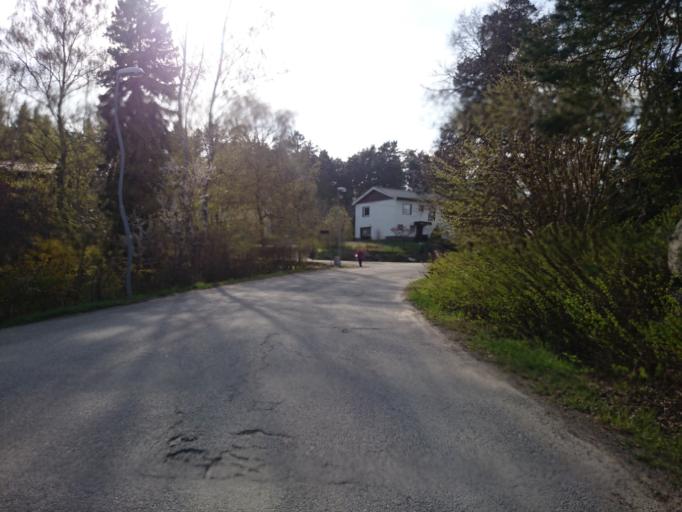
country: SE
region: Stockholm
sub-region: Huddinge Kommun
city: Huddinge
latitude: 59.2409
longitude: 18.0229
